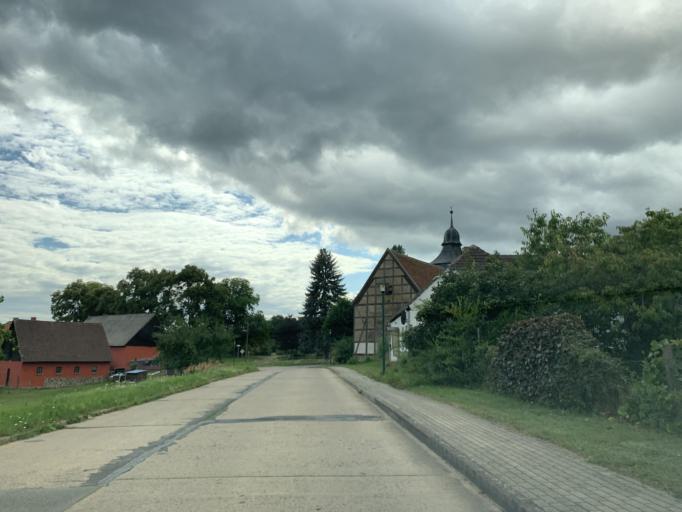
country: DE
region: Mecklenburg-Vorpommern
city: Carpin
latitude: 53.3783
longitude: 13.1819
